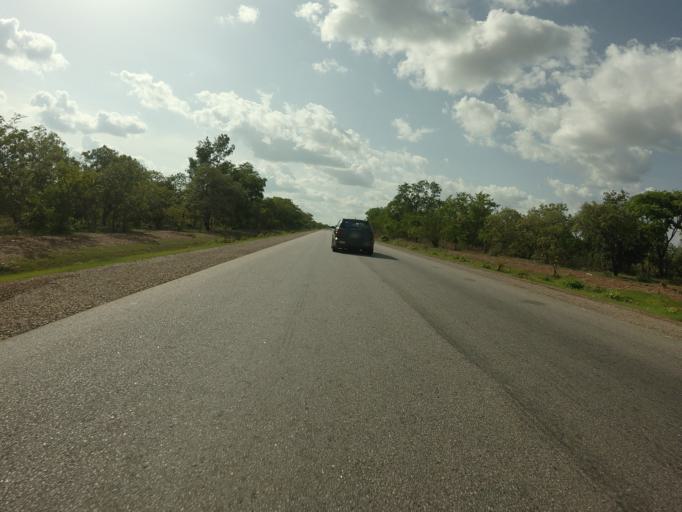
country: GH
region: Upper East
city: Bolgatanga
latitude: 10.5283
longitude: -0.8168
